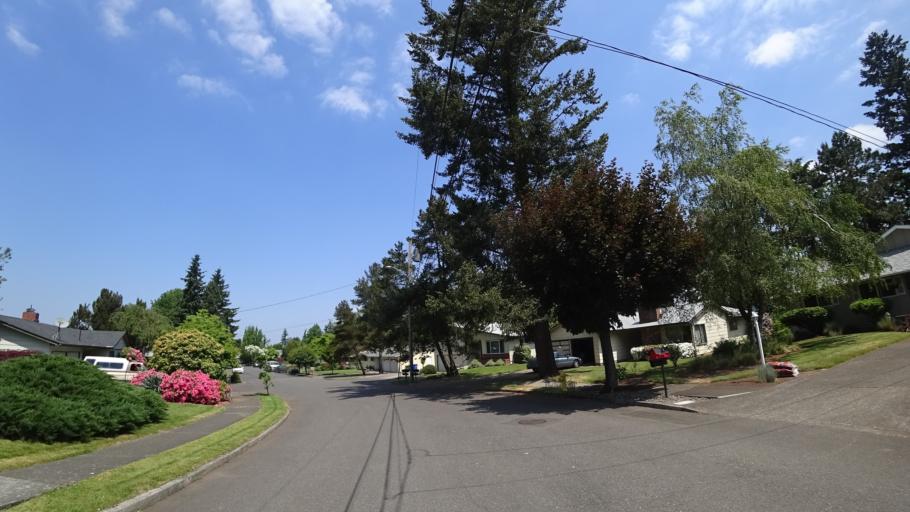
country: US
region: Oregon
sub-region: Multnomah County
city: Fairview
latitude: 45.5350
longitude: -122.4991
